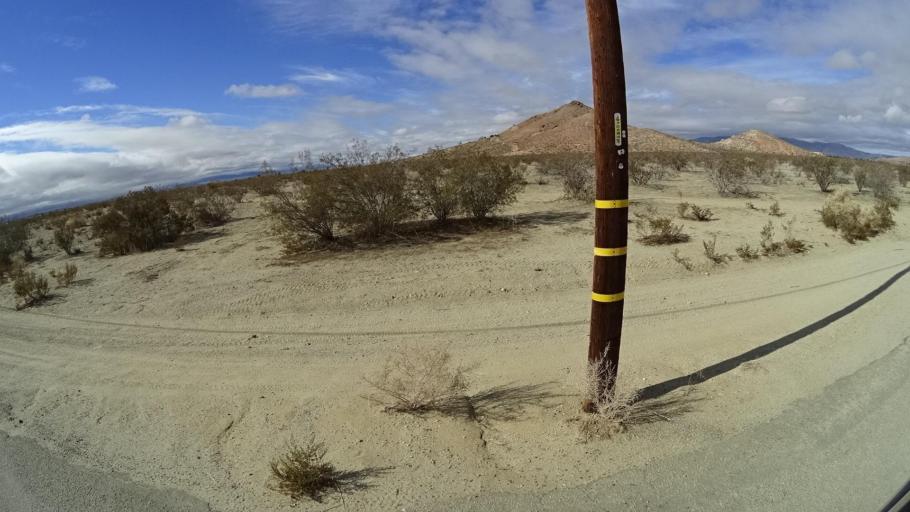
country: US
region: California
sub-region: Kern County
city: Rosamond
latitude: 34.8775
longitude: -118.2202
